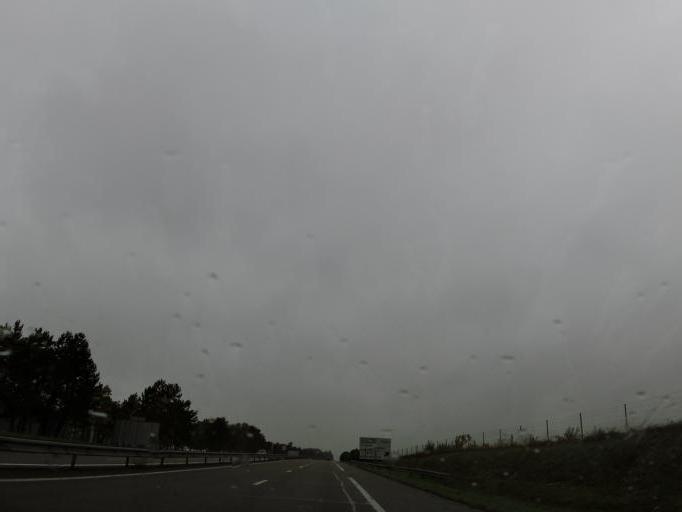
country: FR
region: Champagne-Ardenne
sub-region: Departement de la Marne
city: Fagnieres
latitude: 49.0404
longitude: 4.3384
